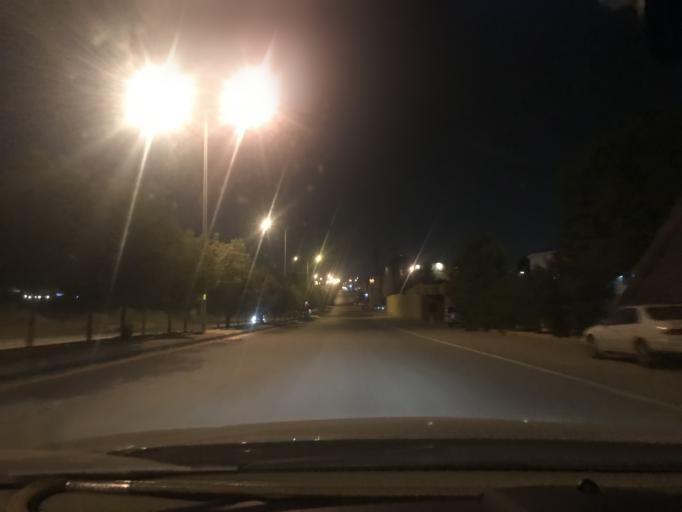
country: SA
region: Ar Riyad
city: Riyadh
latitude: 24.7533
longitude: 46.7546
